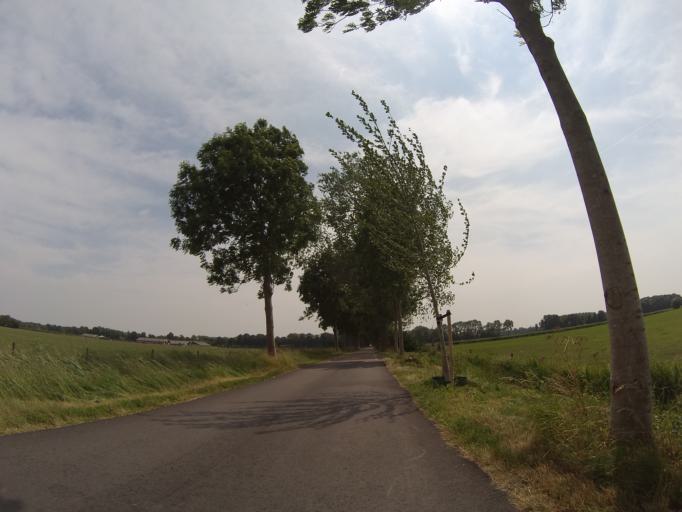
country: NL
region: Utrecht
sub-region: Gemeente Zeist
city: Zeist
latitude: 52.0684
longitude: 5.2333
